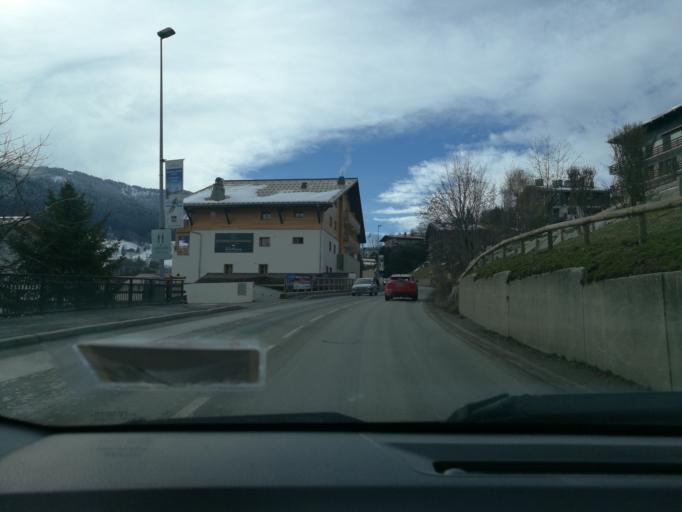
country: FR
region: Rhone-Alpes
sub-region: Departement de la Haute-Savoie
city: Combloux
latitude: 45.8933
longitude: 6.6454
